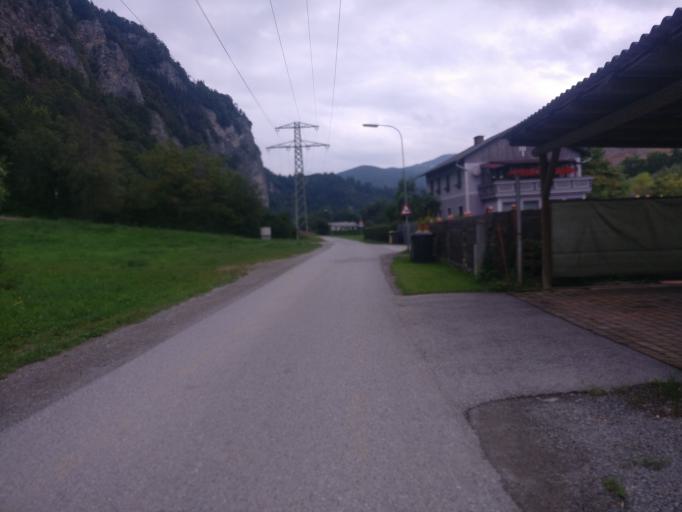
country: AT
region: Styria
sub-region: Politischer Bezirk Graz-Umgebung
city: Peggau
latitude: 47.2122
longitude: 15.3358
